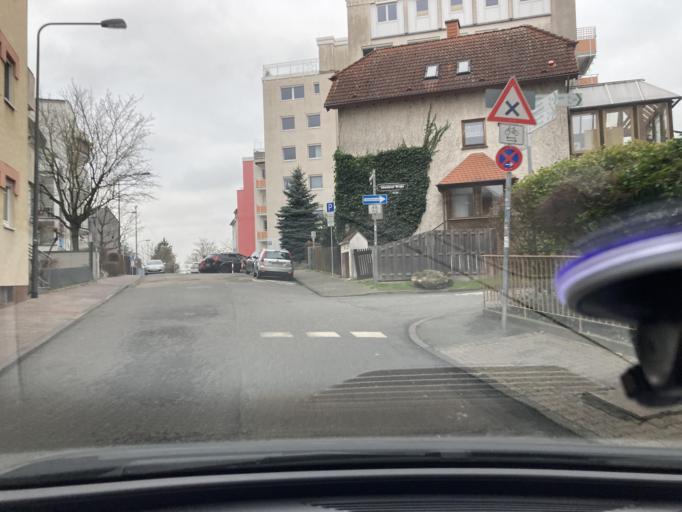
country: DE
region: Hesse
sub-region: Regierungsbezirk Darmstadt
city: Frankfurt am Main
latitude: 50.1328
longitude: 8.7162
